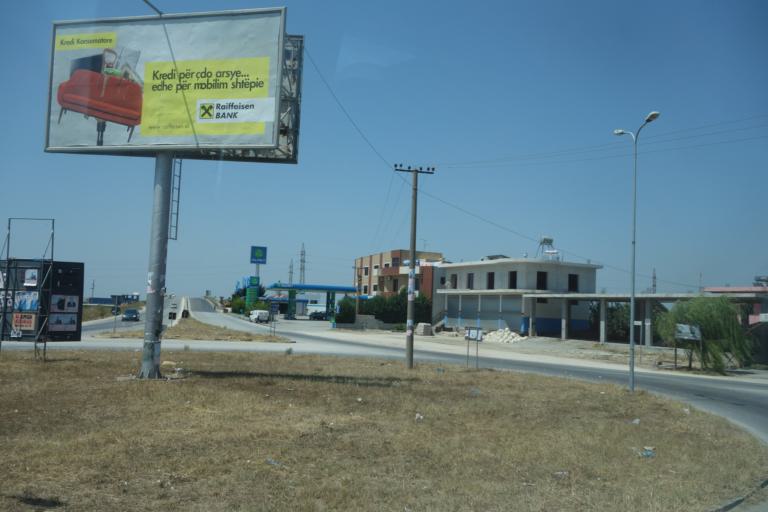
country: AL
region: Fier
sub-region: Rrethi i Lushnjes
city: Karbunara e Vogel
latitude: 40.9207
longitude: 19.7021
